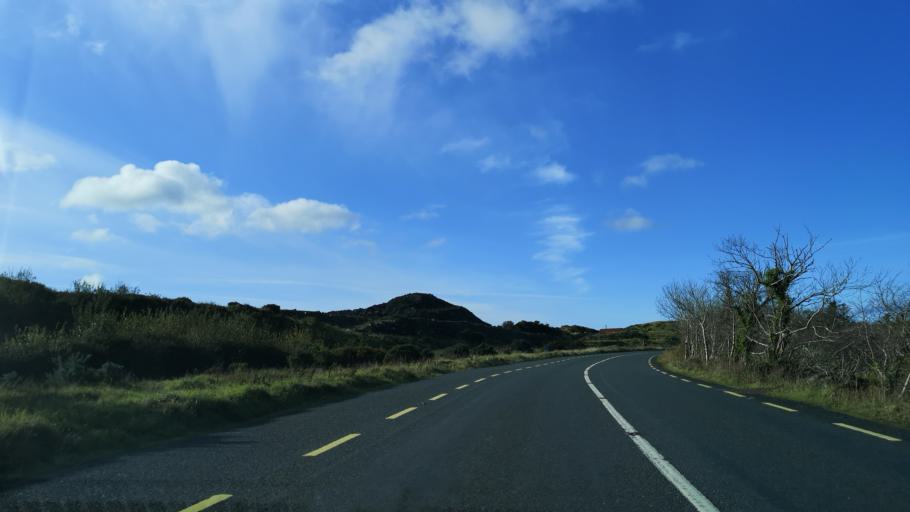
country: IE
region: Connaught
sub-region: County Galway
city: Clifden
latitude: 53.5607
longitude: -9.9188
